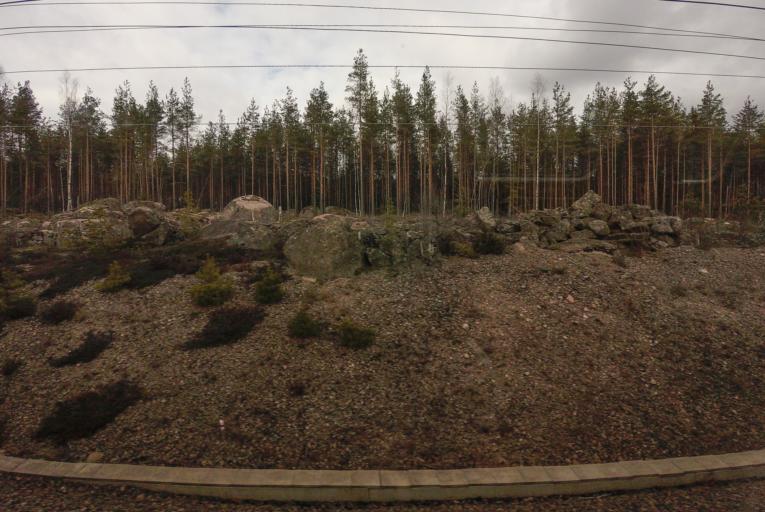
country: FI
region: Paijanne Tavastia
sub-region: Lahti
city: Artjaervi
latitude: 60.9241
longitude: 26.1278
